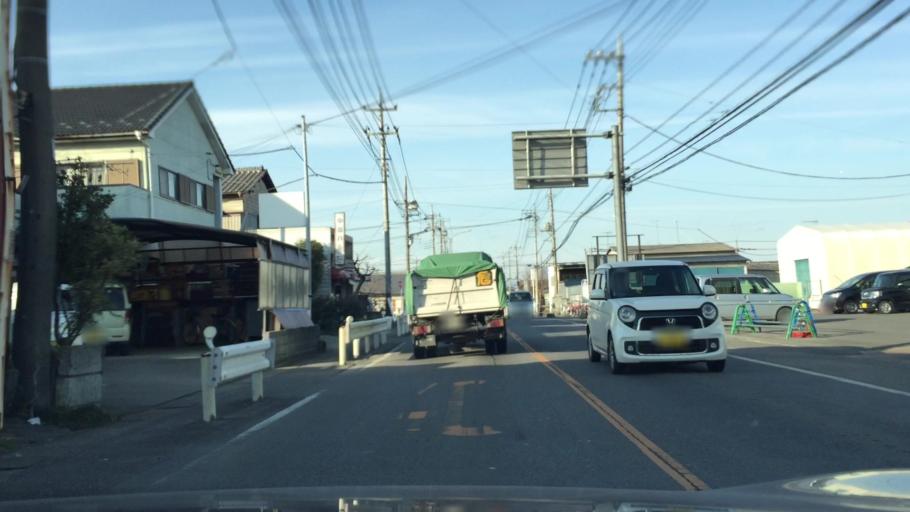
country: JP
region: Saitama
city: Menuma
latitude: 36.2024
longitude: 139.3743
